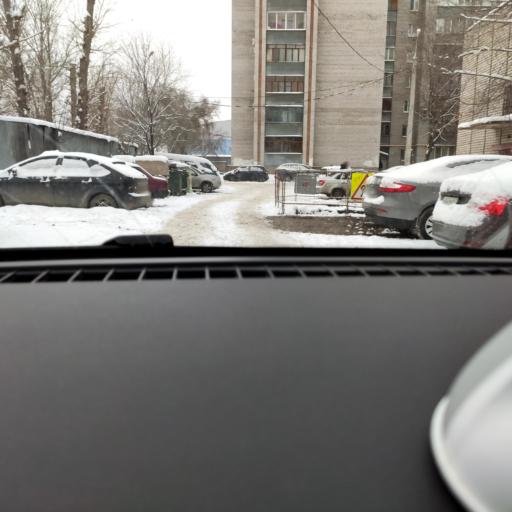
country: RU
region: Samara
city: Samara
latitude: 53.2098
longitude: 50.2546
